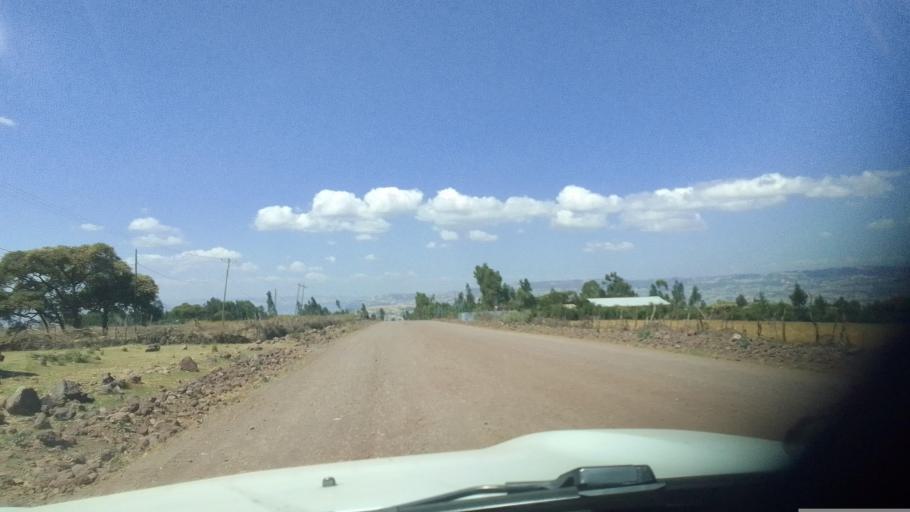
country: ET
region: Oromiya
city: Hagere Hiywet
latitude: 8.9206
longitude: 37.8661
